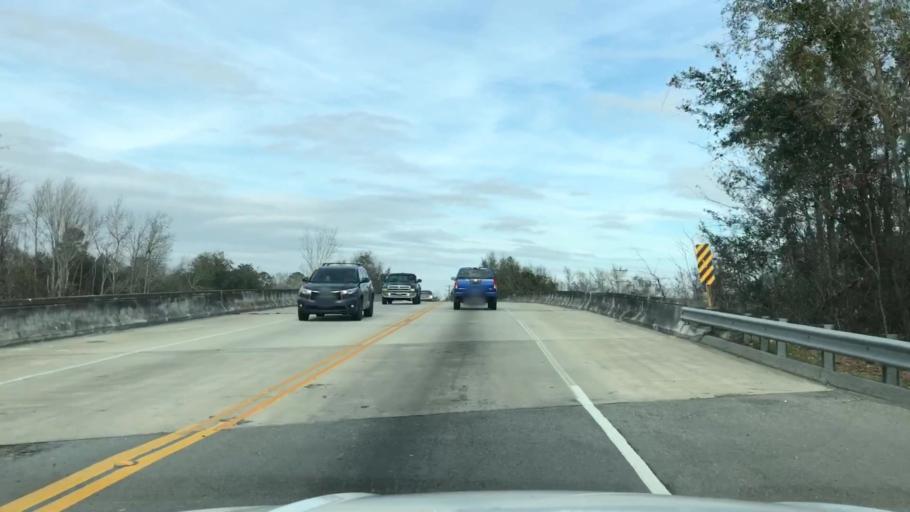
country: US
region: South Carolina
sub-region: Charleston County
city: Shell Point
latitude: 32.7921
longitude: -80.1079
